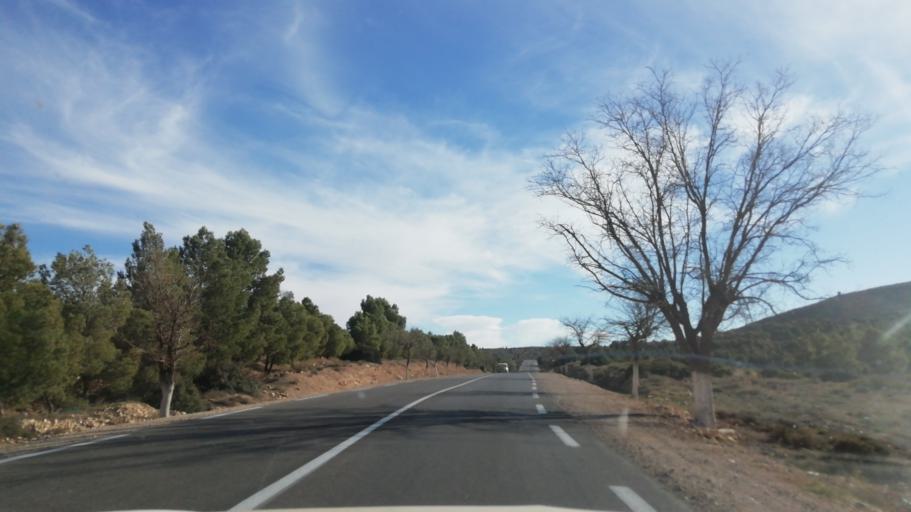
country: DZ
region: Tlemcen
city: Sebdou
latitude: 34.5927
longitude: -1.3190
